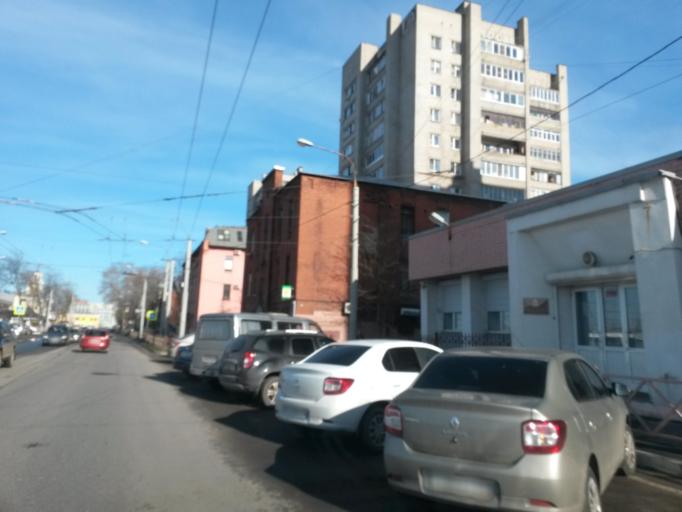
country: RU
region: Jaroslavl
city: Yaroslavl
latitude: 57.6243
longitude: 39.8403
